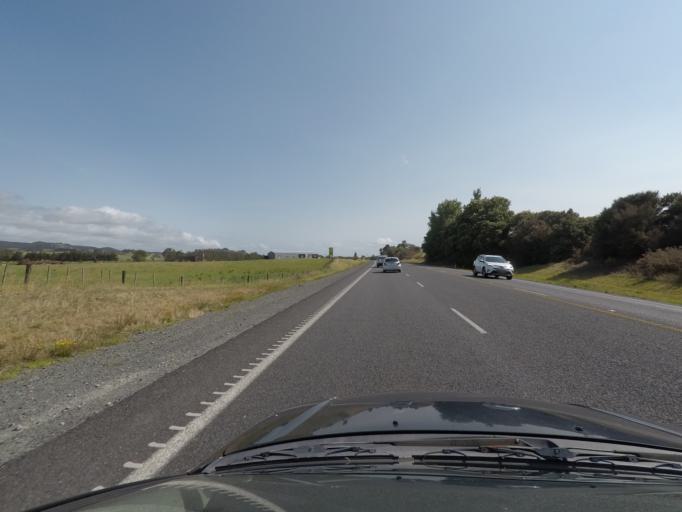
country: NZ
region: Northland
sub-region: Whangarei
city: Ruakaka
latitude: -35.9539
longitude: 174.4523
